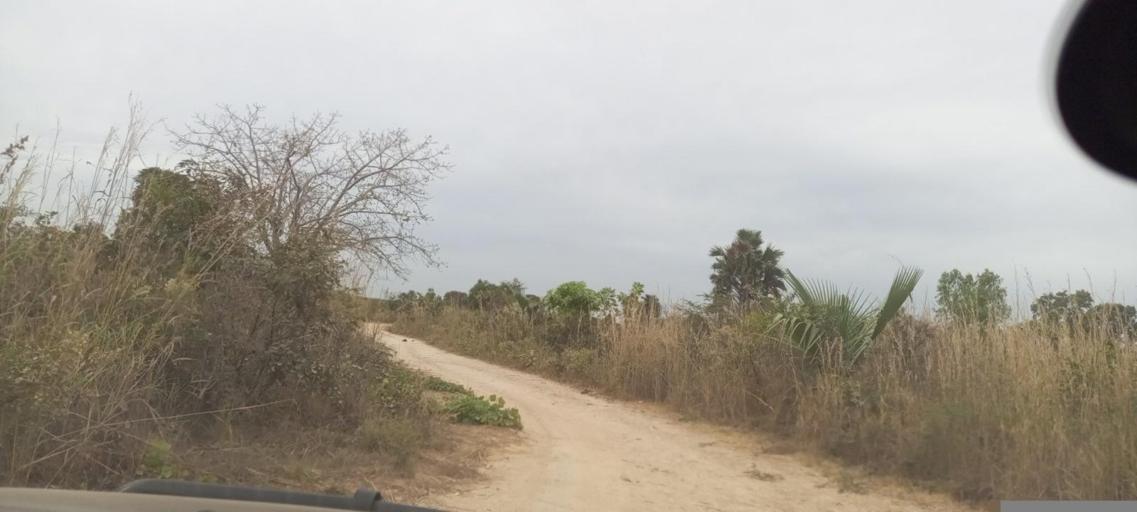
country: ML
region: Koulikoro
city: Kati
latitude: 12.7564
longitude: -8.3070
